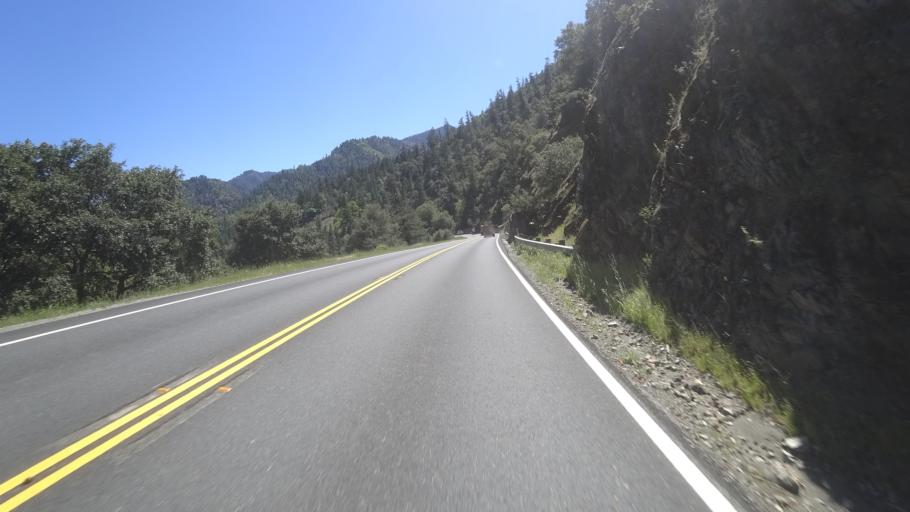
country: US
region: California
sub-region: Humboldt County
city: Willow Creek
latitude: 40.7927
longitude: -123.4560
